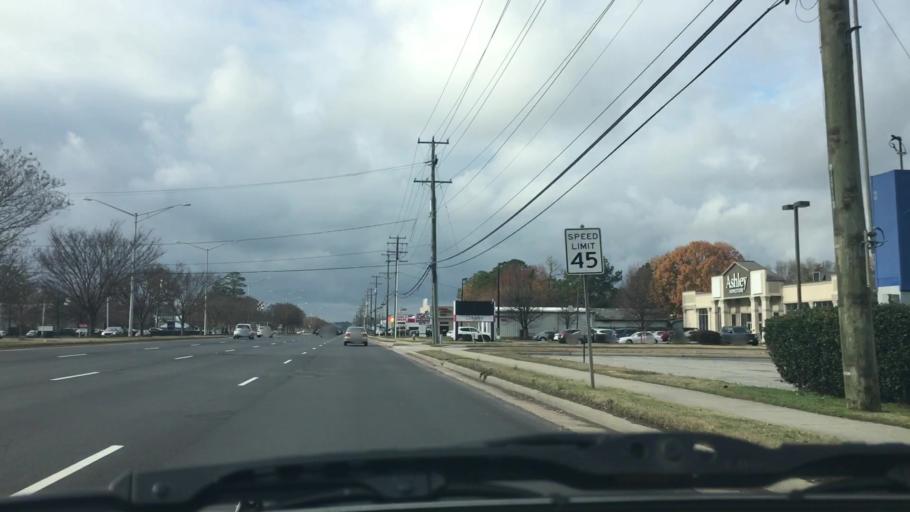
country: US
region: Virginia
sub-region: City of Chesapeake
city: Chesapeake
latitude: 36.8463
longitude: -76.1576
